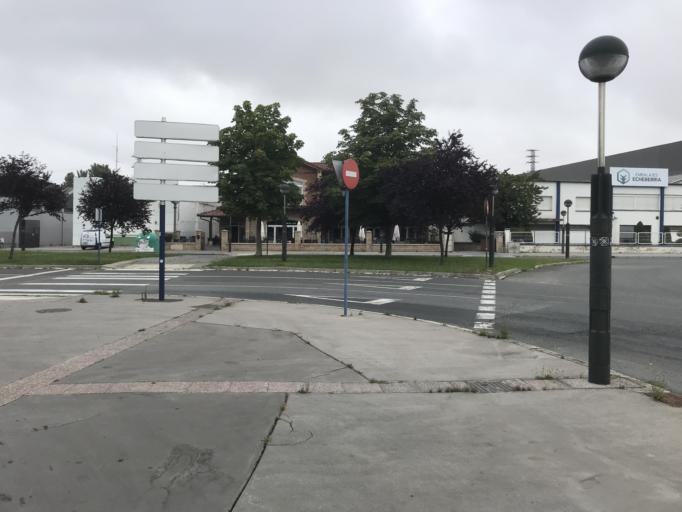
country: ES
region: Basque Country
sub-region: Provincia de Alava
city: Gasteiz / Vitoria
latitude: 42.8637
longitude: -2.6489
